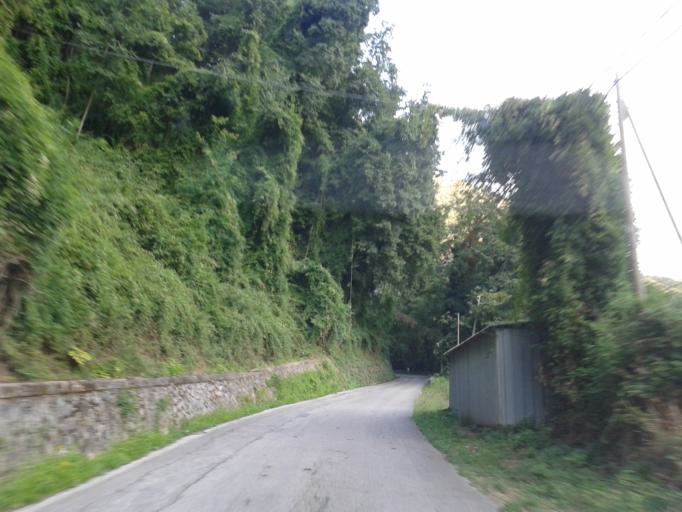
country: IT
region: Tuscany
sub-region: Provincia di Lucca
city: Pontestazzemese
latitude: 43.9659
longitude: 10.3315
